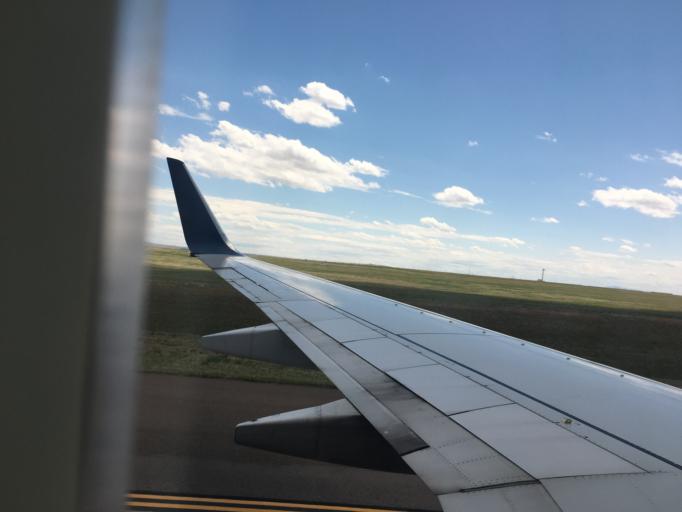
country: US
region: Colorado
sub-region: Weld County
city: Lochbuie
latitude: 39.8566
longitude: -104.6509
